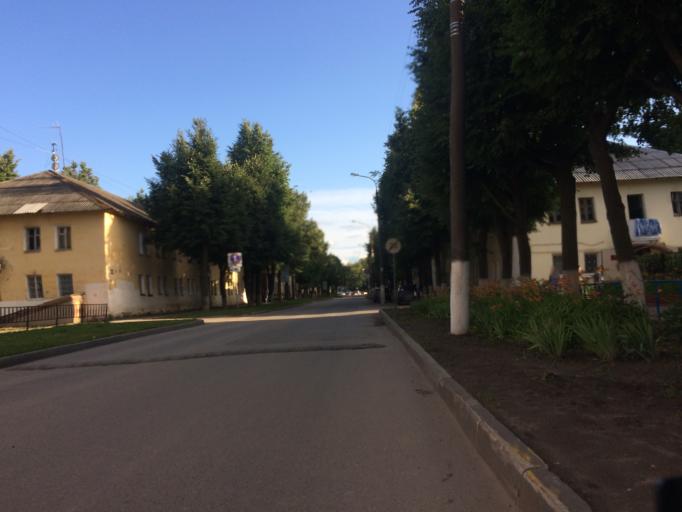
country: RU
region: Mariy-El
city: Yoshkar-Ola
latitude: 56.6355
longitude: 47.8804
